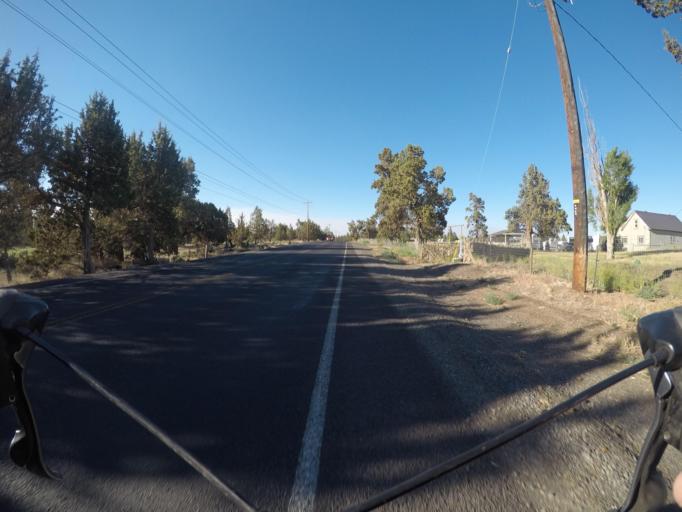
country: US
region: Oregon
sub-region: Deschutes County
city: Redmond
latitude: 44.2275
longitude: -121.2297
